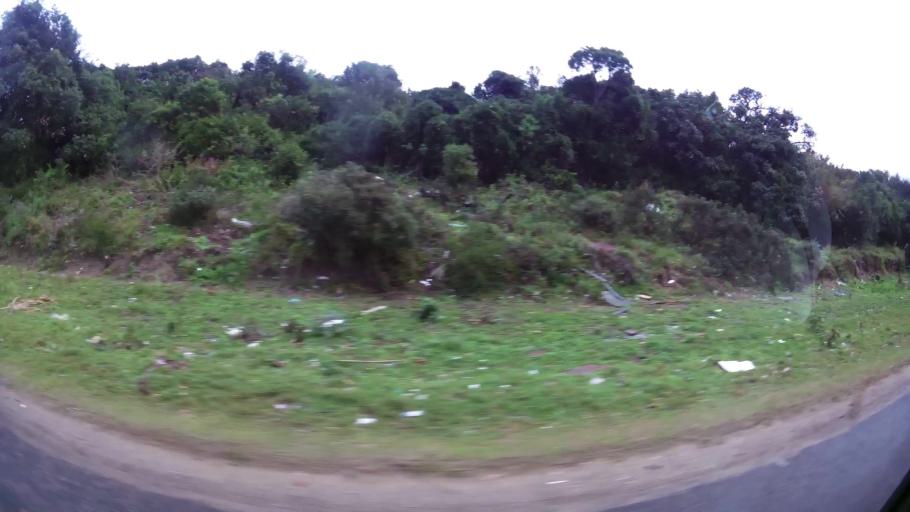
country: ZA
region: Eastern Cape
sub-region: Nelson Mandela Bay Metropolitan Municipality
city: Port Elizabeth
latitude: -33.9986
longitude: 25.5773
